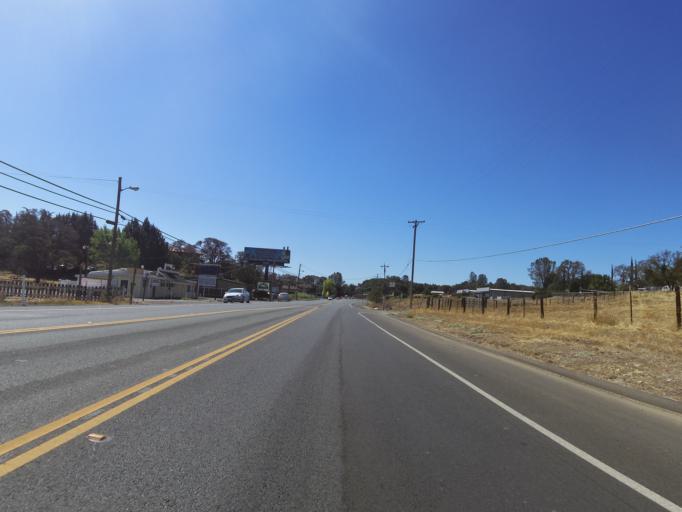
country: US
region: California
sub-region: Amador County
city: Plymouth
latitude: 38.4687
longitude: -120.8538
